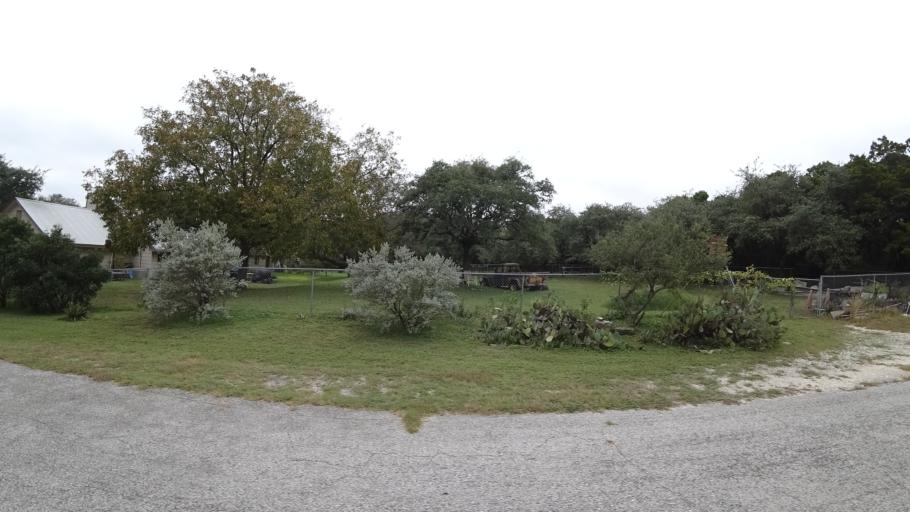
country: US
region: Texas
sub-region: Travis County
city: Barton Creek
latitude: 30.2512
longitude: -97.9163
